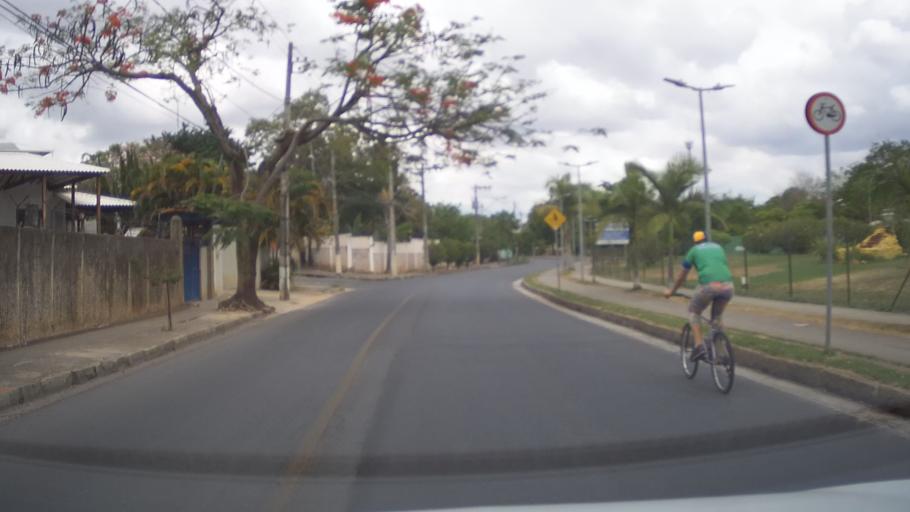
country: BR
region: Minas Gerais
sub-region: Belo Horizonte
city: Belo Horizonte
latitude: -19.8568
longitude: -43.9949
